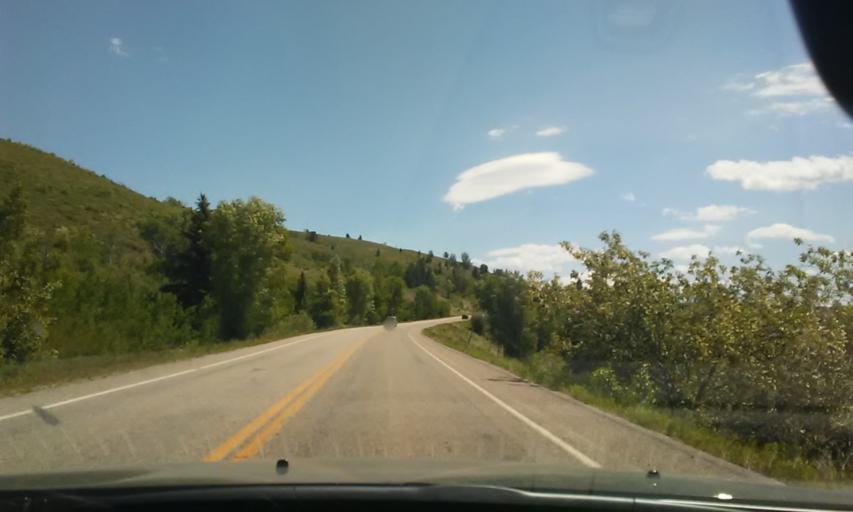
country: US
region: Wyoming
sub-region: Teton County
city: Jackson
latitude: 43.8388
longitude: -110.4920
